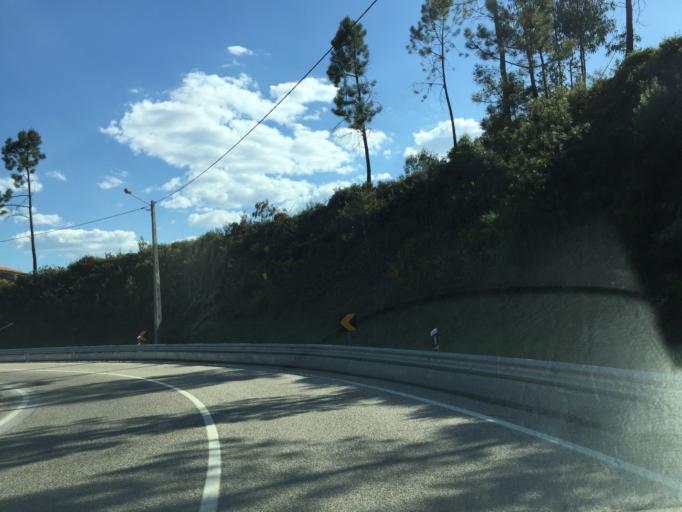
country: PT
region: Leiria
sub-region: Pedrogao Grande
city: Pedrogao Grande
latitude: 39.9102
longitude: -8.1527
